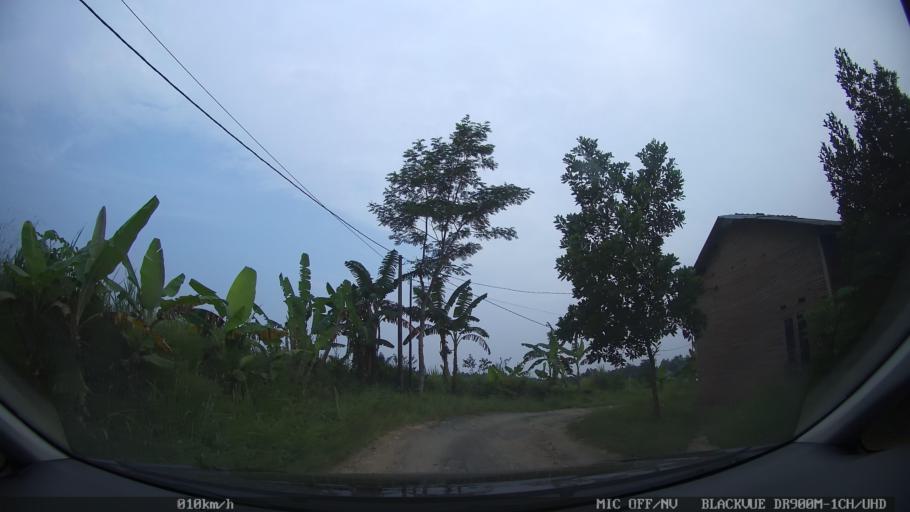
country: ID
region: Lampung
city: Panjang
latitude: -5.4229
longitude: 105.3459
